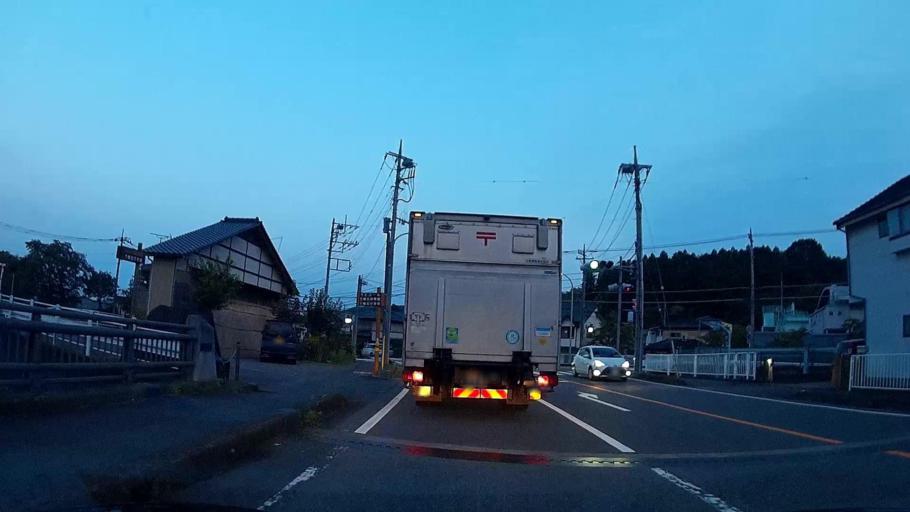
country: JP
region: Gunma
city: Annaka
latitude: 36.3803
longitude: 138.8839
